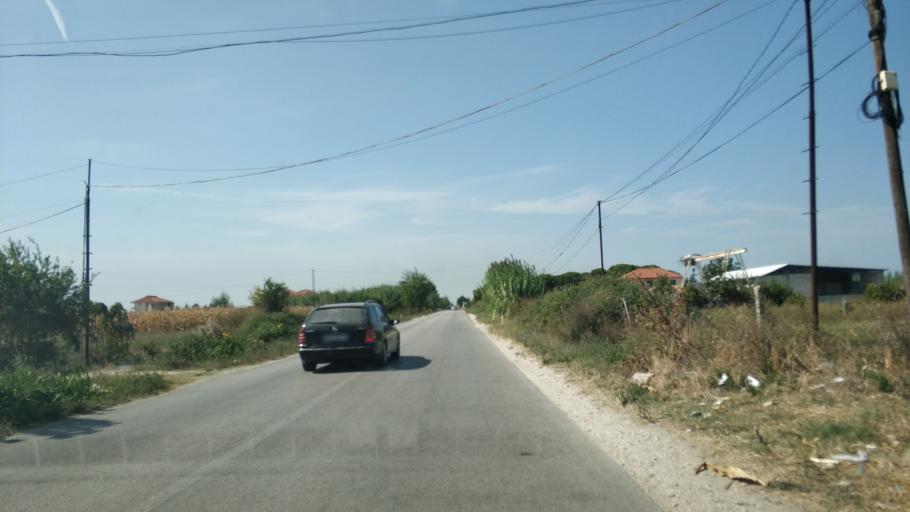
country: AL
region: Fier
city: Fier
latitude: 40.7344
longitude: 19.5283
